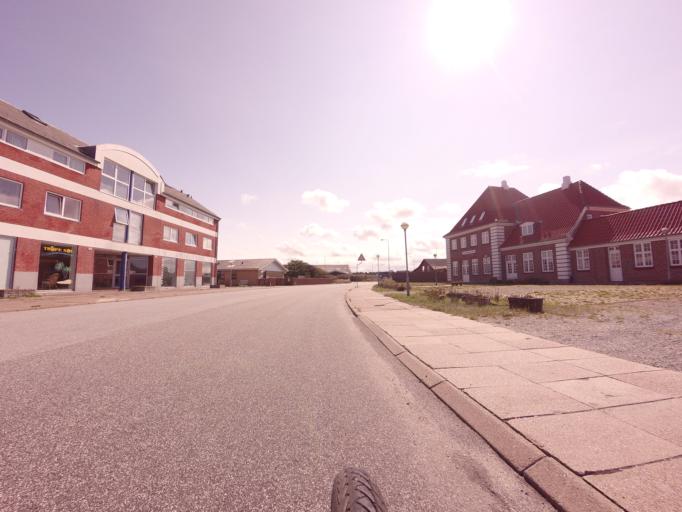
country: DK
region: North Denmark
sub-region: Hjorring Kommune
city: Hirtshals
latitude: 57.5888
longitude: 9.9703
